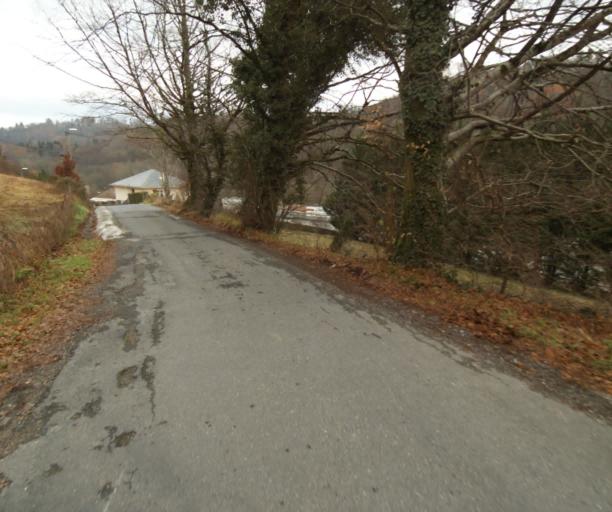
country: FR
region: Limousin
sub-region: Departement de la Correze
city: Tulle
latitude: 45.2426
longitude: 1.7418
